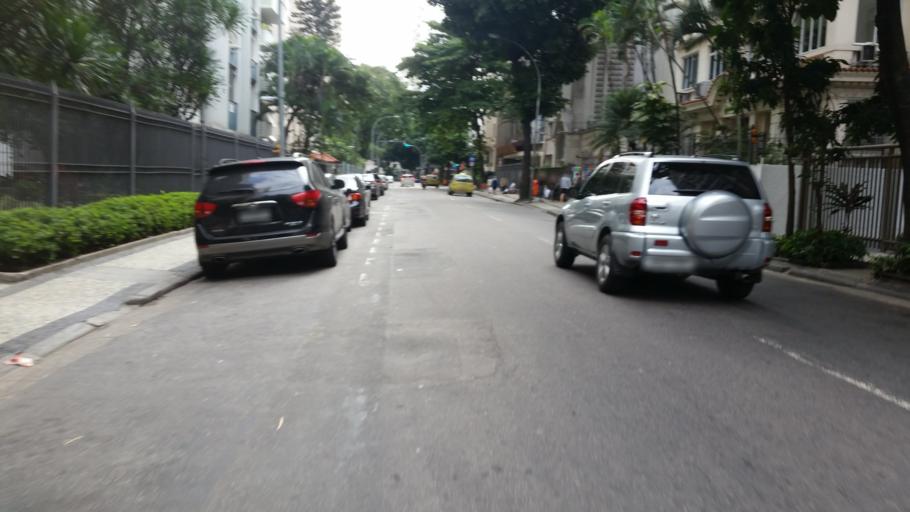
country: BR
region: Rio de Janeiro
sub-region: Rio De Janeiro
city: Rio de Janeiro
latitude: -22.9377
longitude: -43.1762
